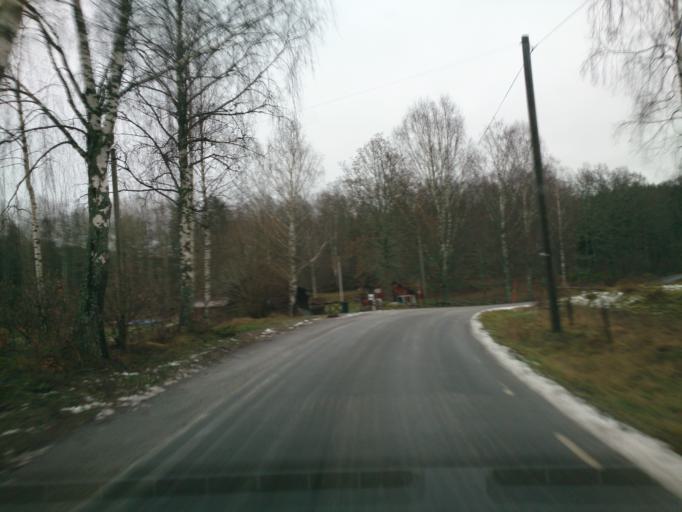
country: SE
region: OEstergoetland
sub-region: Atvidabergs Kommun
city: Atvidaberg
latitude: 58.2816
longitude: 16.1496
